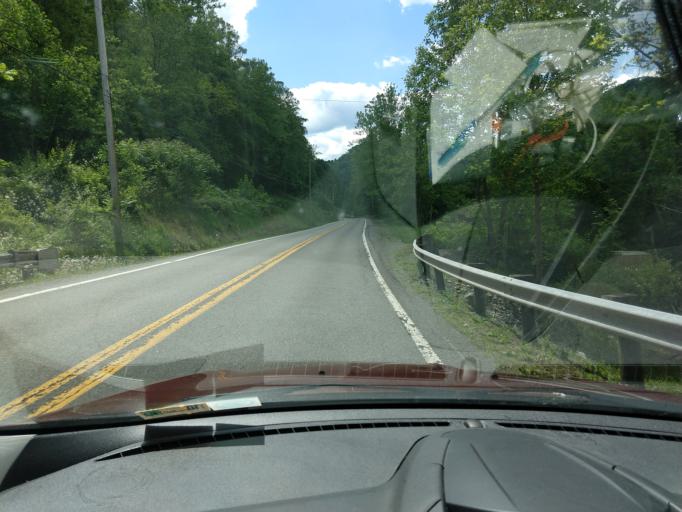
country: US
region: West Virginia
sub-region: Gilmer County
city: Glenville
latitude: 38.8716
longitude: -80.6986
